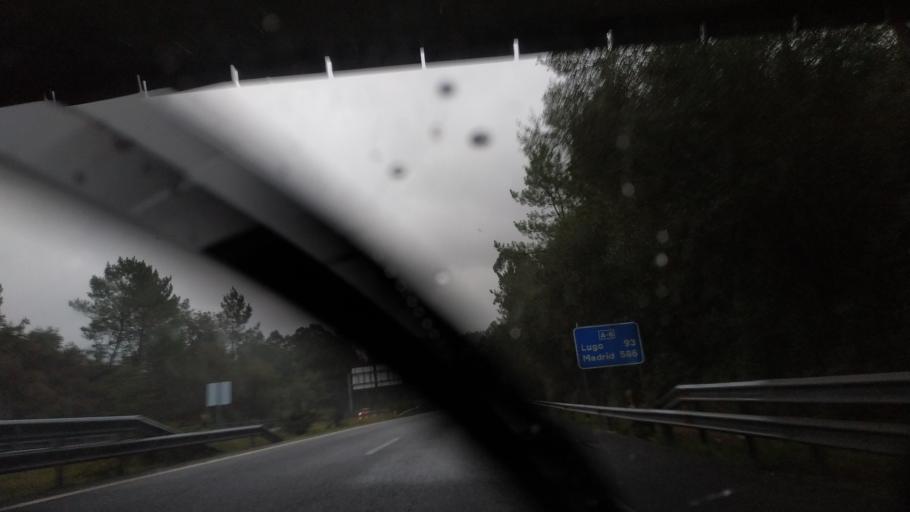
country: ES
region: Galicia
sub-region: Provincia da Coruna
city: Culleredo
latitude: 43.2705
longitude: -8.3934
